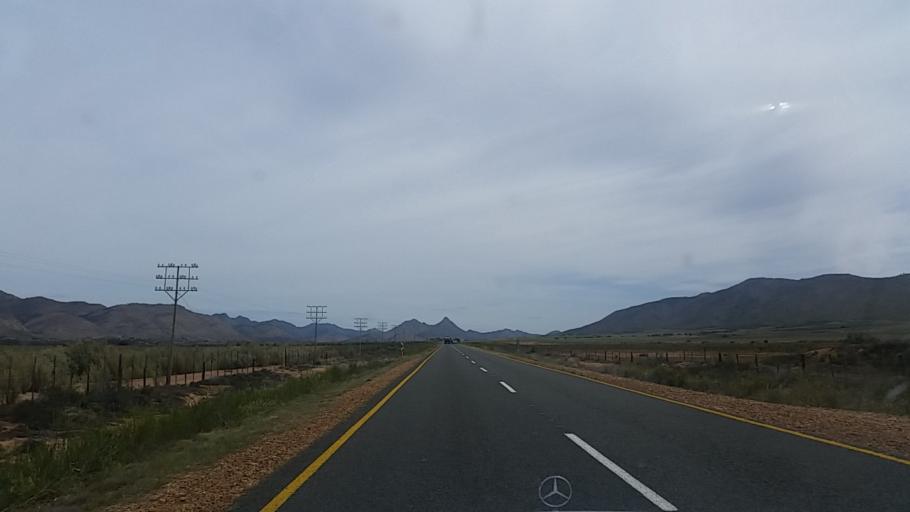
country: ZA
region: Western Cape
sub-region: Eden District Municipality
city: George
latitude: -33.8098
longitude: 22.5448
